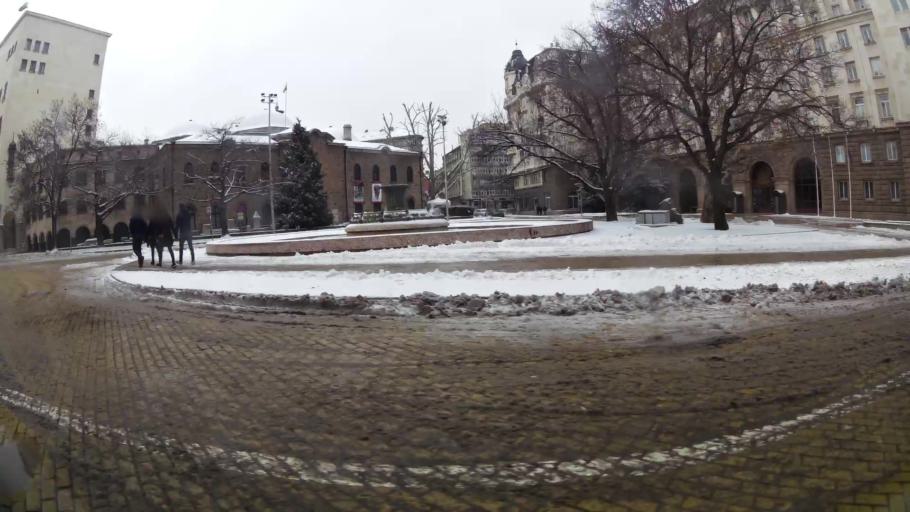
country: BG
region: Sofia-Capital
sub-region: Stolichna Obshtina
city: Sofia
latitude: 42.6970
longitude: 23.3246
